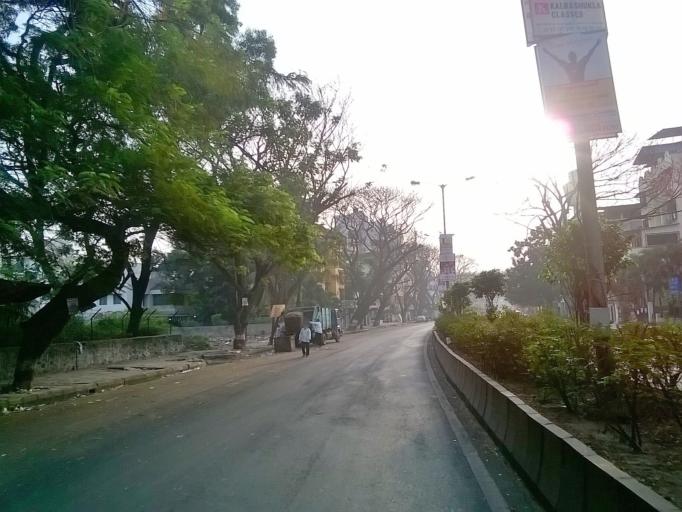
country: IN
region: Maharashtra
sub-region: Raigarh
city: Panvel
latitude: 18.9972
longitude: 73.1201
